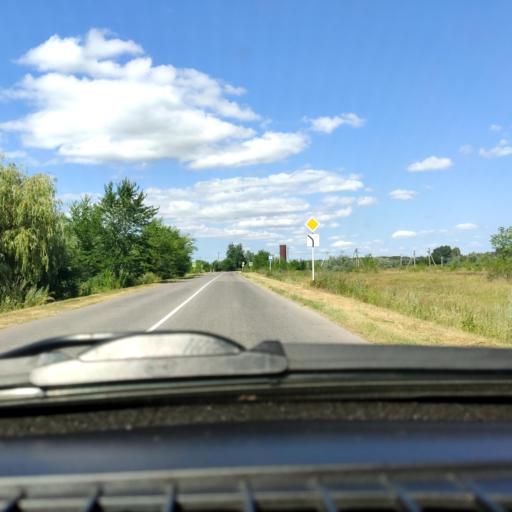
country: RU
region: Samara
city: Tol'yatti
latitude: 53.7184
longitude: 49.4235
